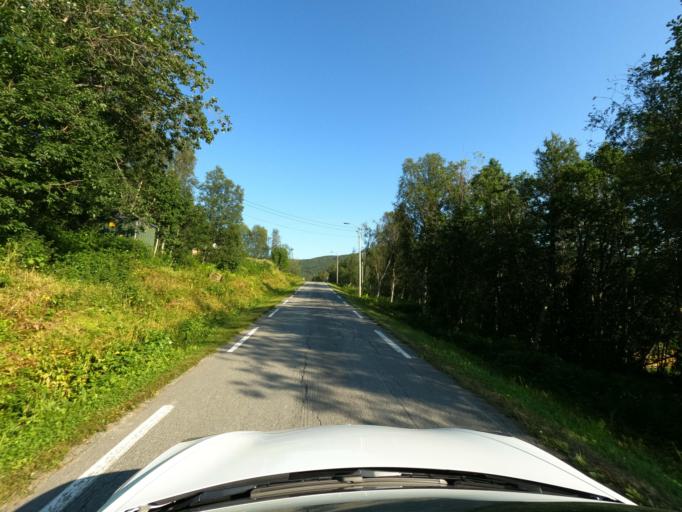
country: NO
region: Troms
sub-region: Gratangen
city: Gratangen
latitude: 68.5578
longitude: 17.7228
